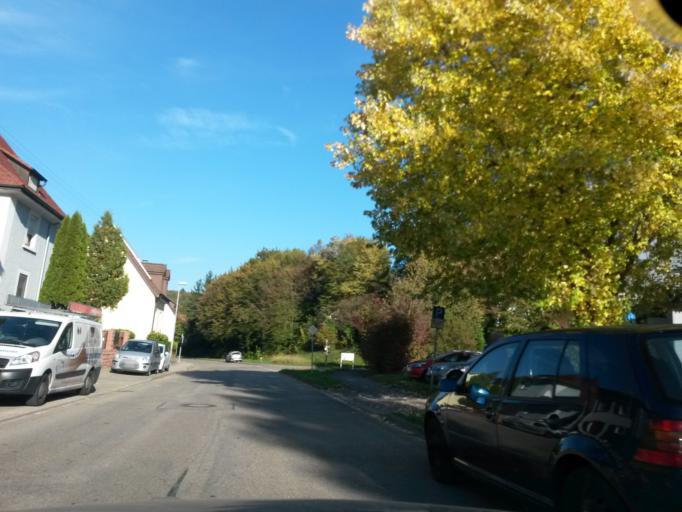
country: DE
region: Baden-Wuerttemberg
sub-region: Karlsruhe Region
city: Konigsbach-Stein
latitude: 48.9401
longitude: 8.5310
